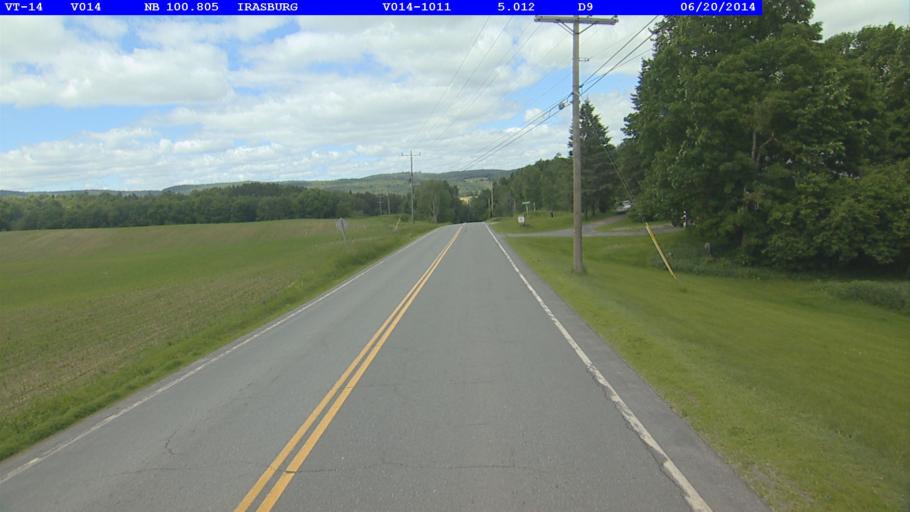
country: US
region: Vermont
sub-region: Orleans County
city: Newport
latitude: 44.8311
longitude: -72.2909
